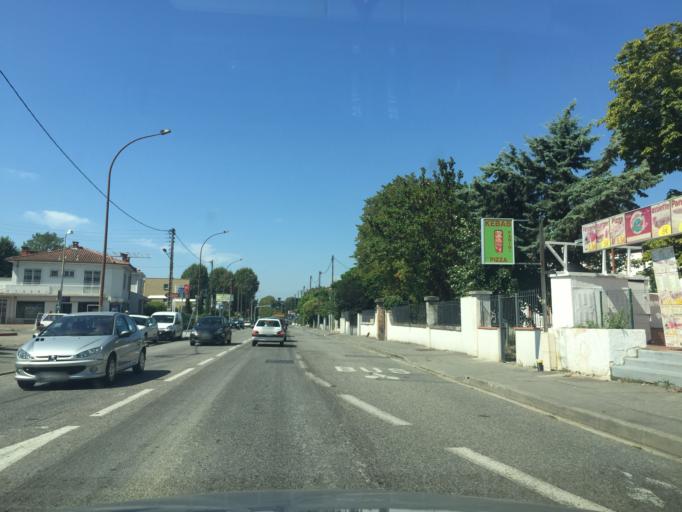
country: FR
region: Midi-Pyrenees
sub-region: Departement de la Haute-Garonne
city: Ramonville-Saint-Agne
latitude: 43.5671
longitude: 1.4583
